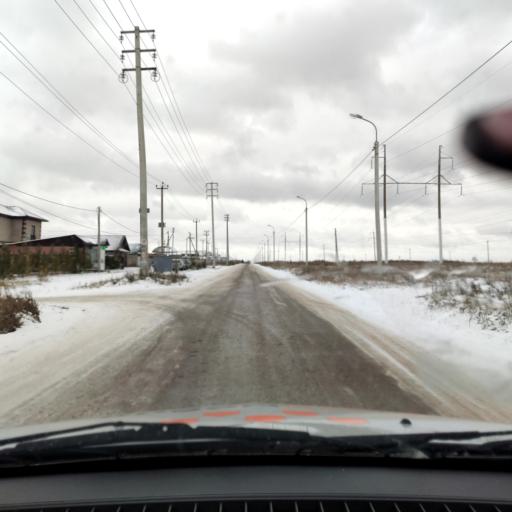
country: RU
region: Bashkortostan
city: Kabakovo
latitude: 54.6138
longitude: 56.0884
